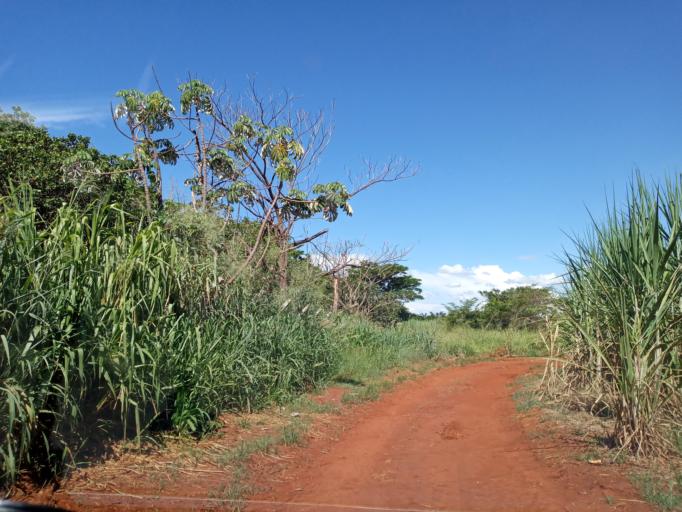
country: BR
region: Goias
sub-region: Itumbiara
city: Itumbiara
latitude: -18.4363
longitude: -49.1174
